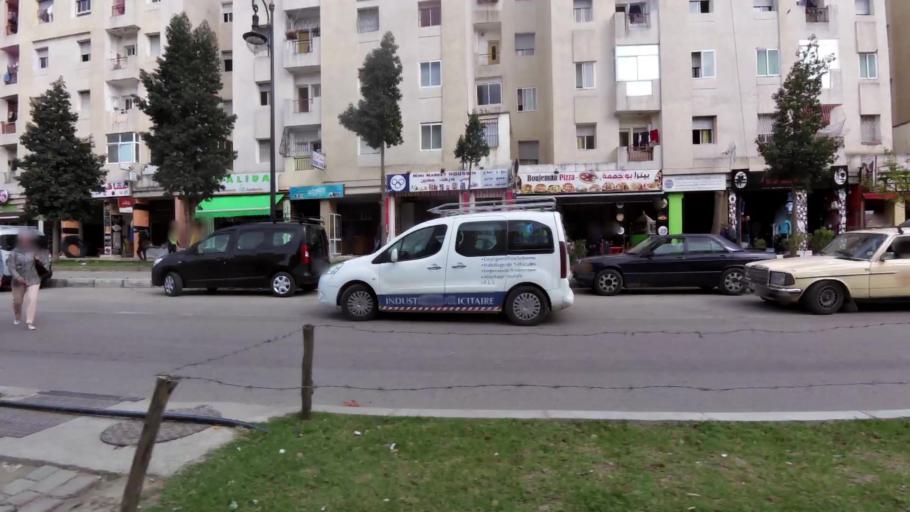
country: MA
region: Tanger-Tetouan
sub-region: Tanger-Assilah
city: Boukhalef
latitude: 35.7334
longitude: -5.8818
